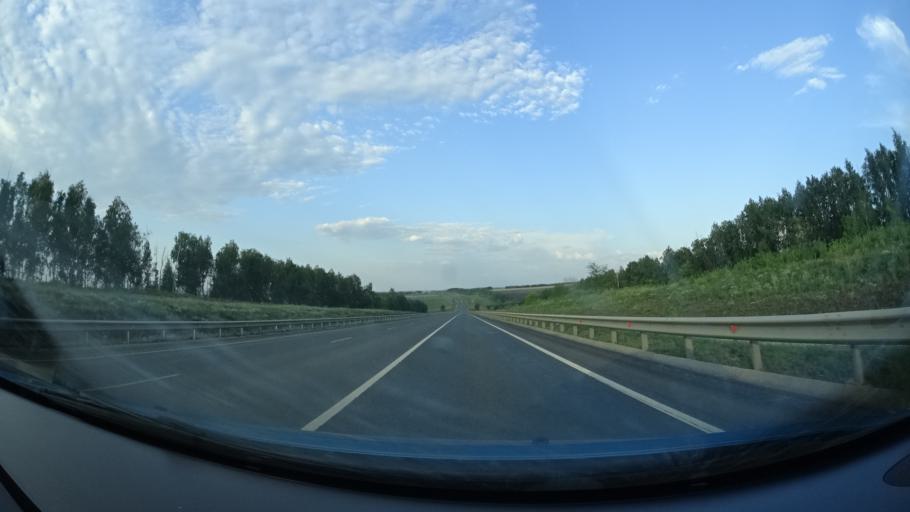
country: RU
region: Samara
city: Klyavlino
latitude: 54.0245
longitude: 51.8664
